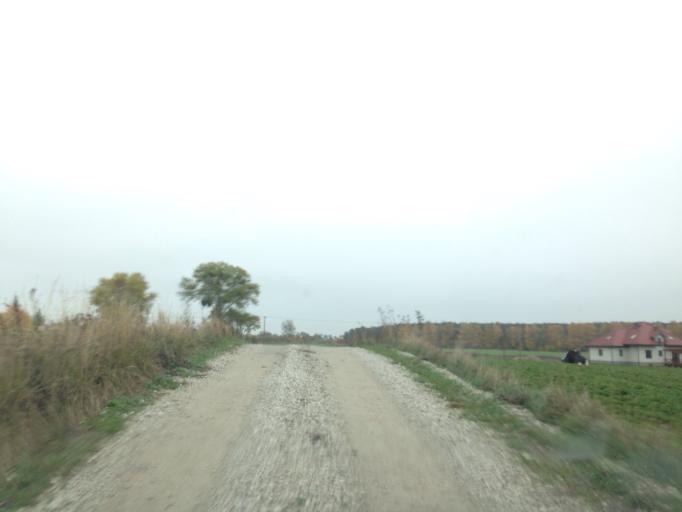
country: PL
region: Kujawsko-Pomorskie
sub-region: Powiat brodnicki
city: Bartniczka
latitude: 53.2158
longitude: 19.6144
